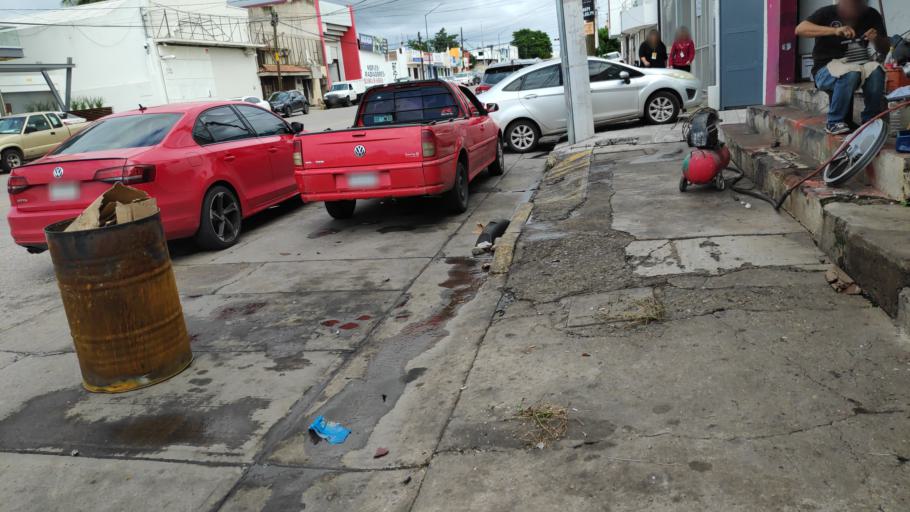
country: MX
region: Sinaloa
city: Culiacan
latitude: 24.7986
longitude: -107.4056
